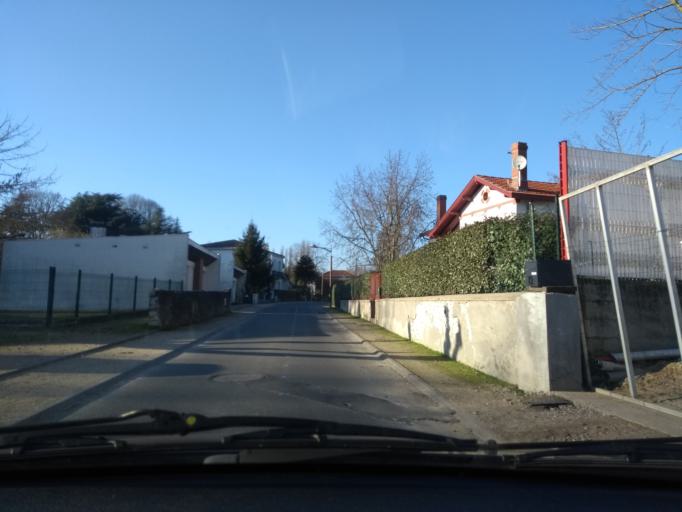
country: FR
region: Aquitaine
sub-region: Departement de la Gironde
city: Salles
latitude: 44.5499
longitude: -0.8717
